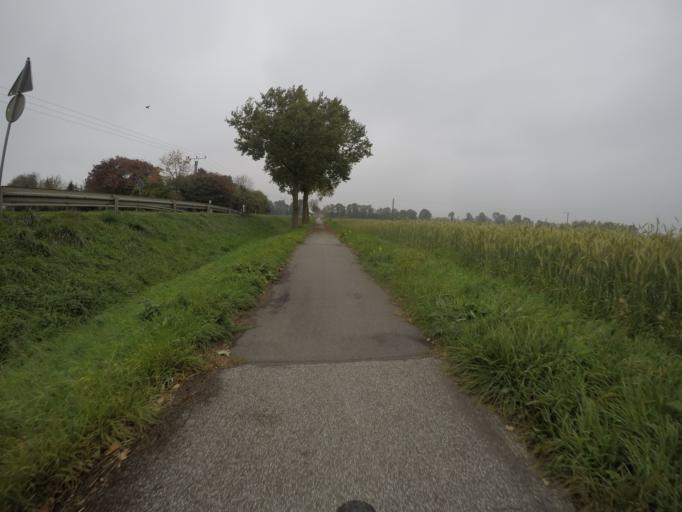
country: DE
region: North Rhine-Westphalia
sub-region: Regierungsbezirk Dusseldorf
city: Bocholt
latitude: 51.8181
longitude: 6.5651
